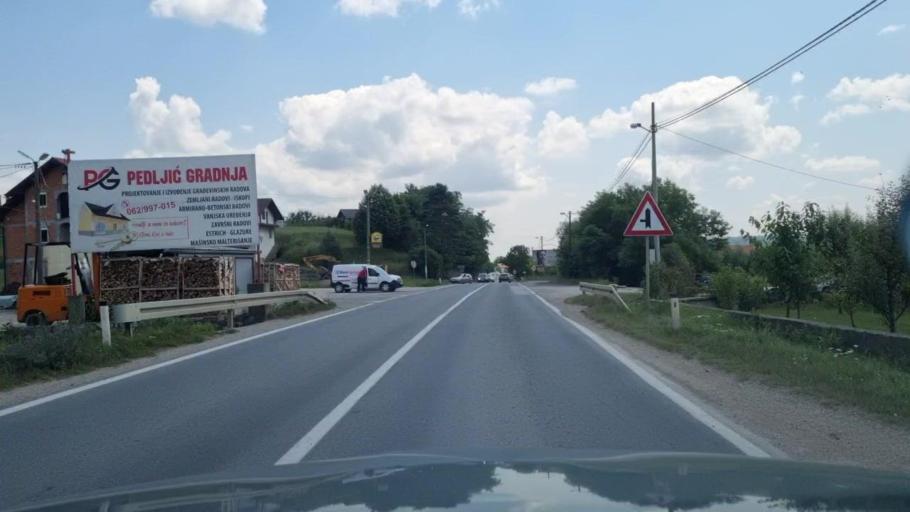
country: BA
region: Federation of Bosnia and Herzegovina
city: Orahovica Donja
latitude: 44.6489
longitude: 18.3617
